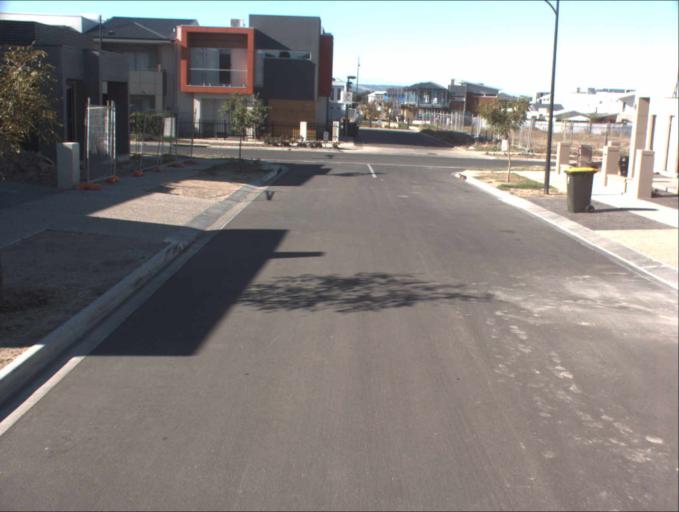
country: AU
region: South Australia
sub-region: Port Adelaide Enfield
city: Klemzig
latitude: -34.8615
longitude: 138.6264
